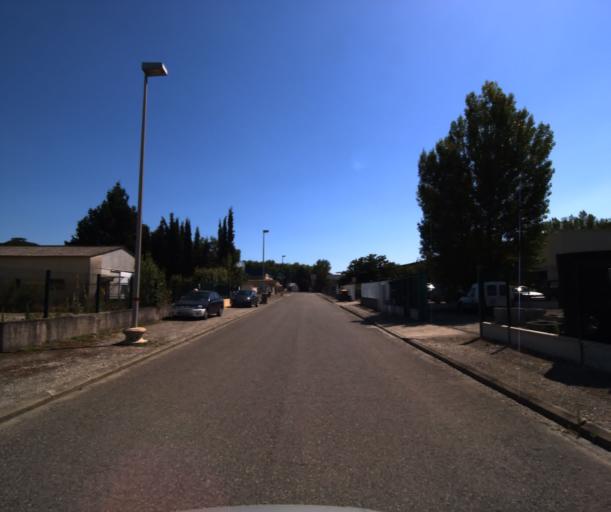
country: FR
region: Midi-Pyrenees
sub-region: Departement de la Haute-Garonne
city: Saubens
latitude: 43.4795
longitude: 1.3418
